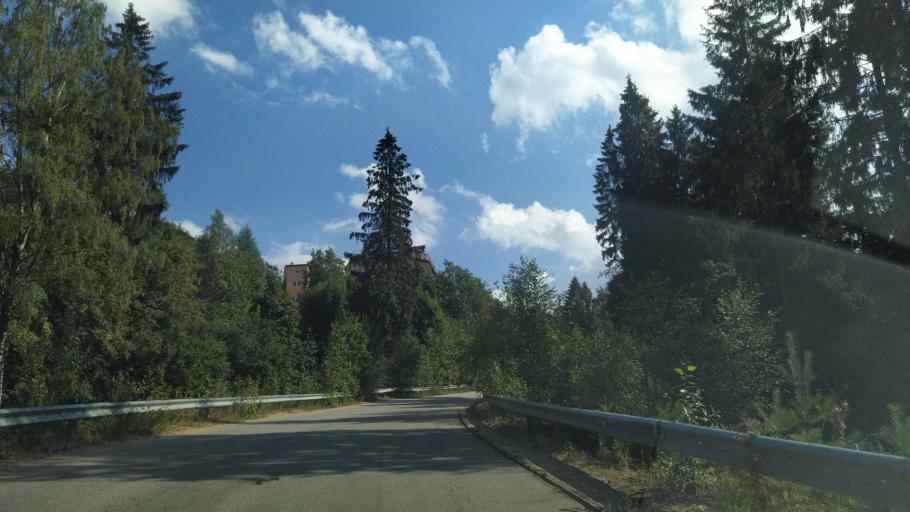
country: RU
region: Leningrad
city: Toksovo
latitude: 60.1672
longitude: 30.5366
